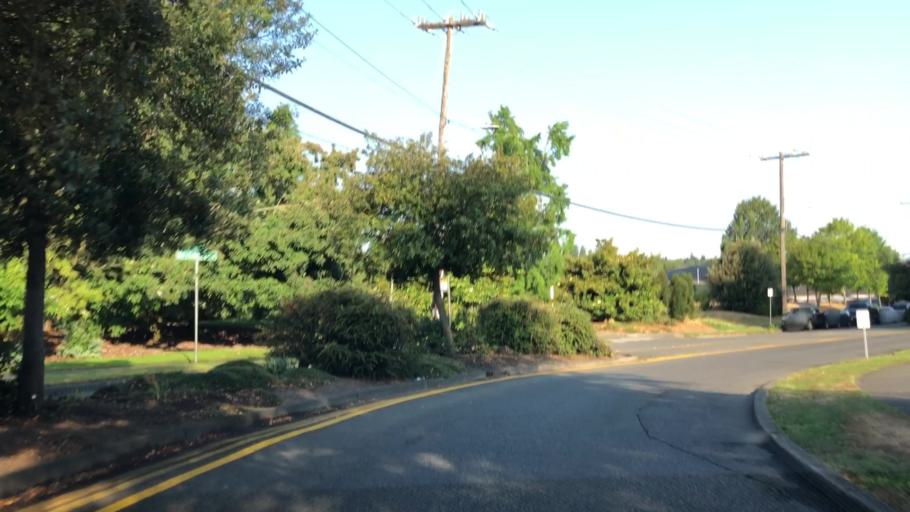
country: US
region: Washington
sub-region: King County
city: Seattle
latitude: 47.6585
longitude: -122.2904
